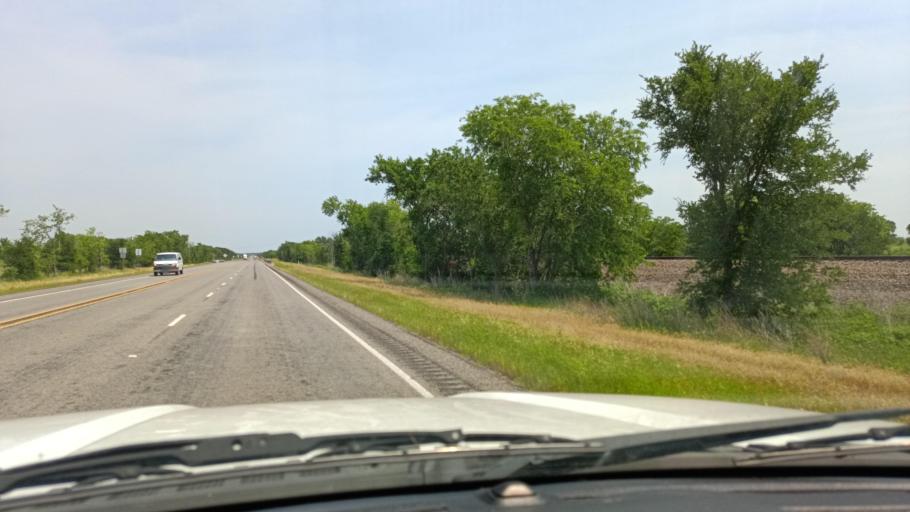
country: US
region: Texas
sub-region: Bell County
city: Rogers
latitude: 30.9041
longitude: -97.1772
